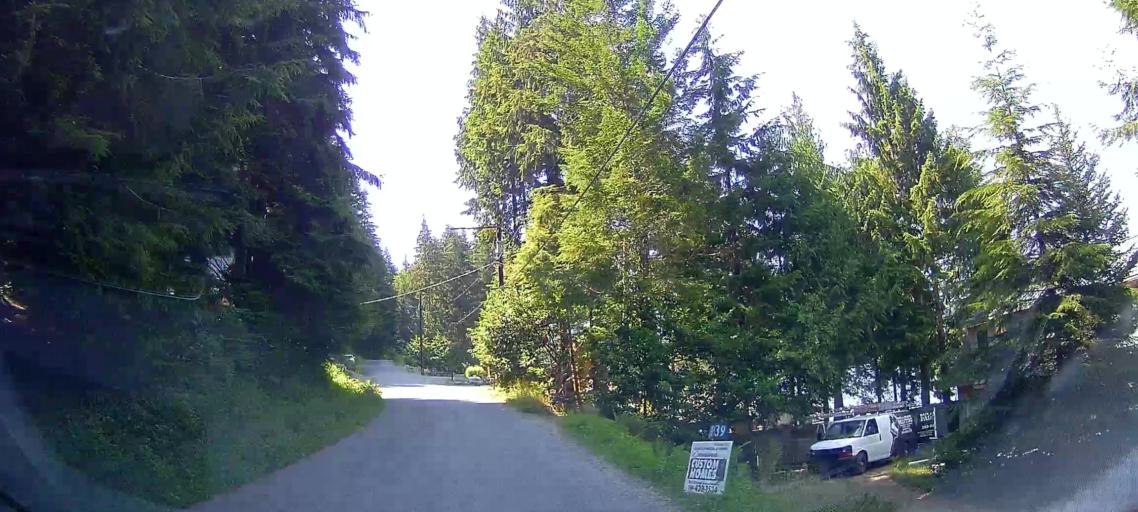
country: US
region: Washington
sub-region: Snohomish County
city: Arlington Heights
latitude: 48.3163
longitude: -122.0113
